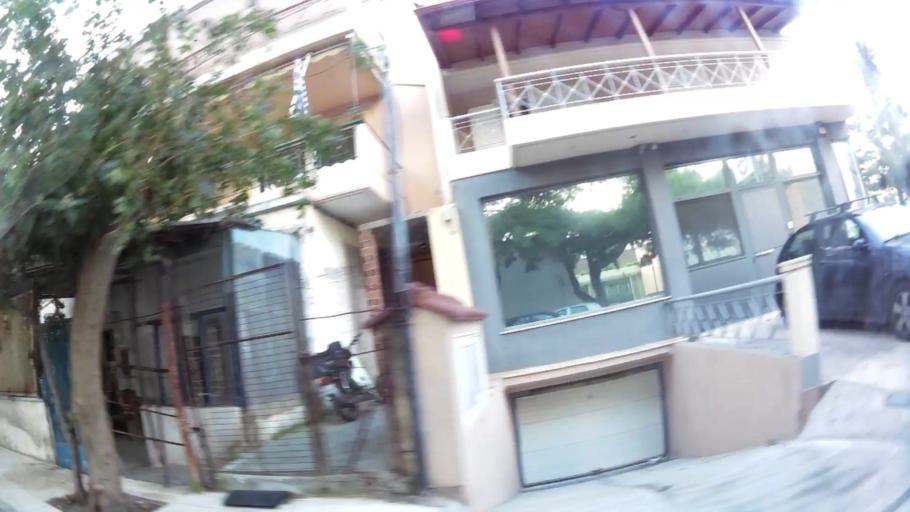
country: GR
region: Attica
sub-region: Nomarchia Athinas
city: Vrilissia
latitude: 38.0413
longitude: 23.8157
